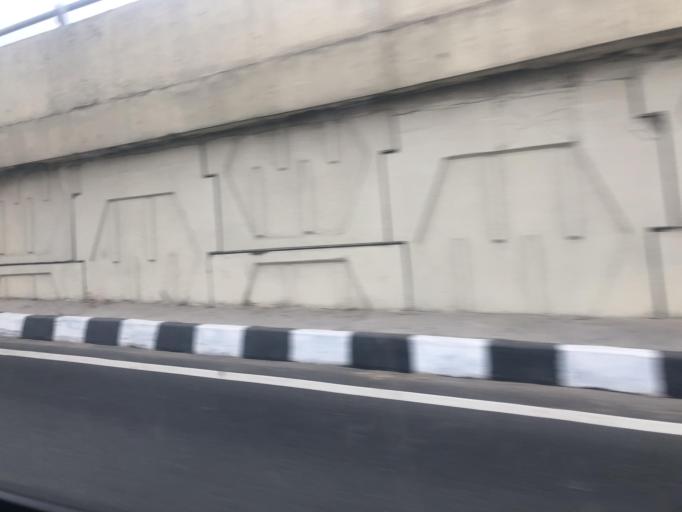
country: IN
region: NCT
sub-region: New Delhi
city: New Delhi
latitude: 28.5993
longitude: 77.2581
